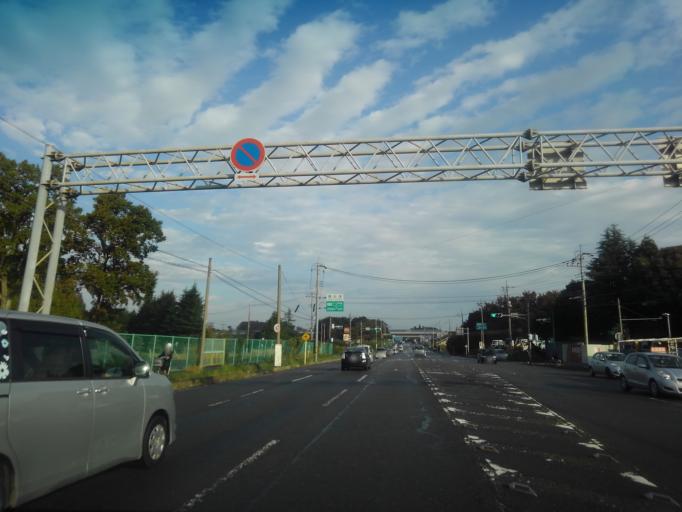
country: JP
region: Ibaraki
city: Naka
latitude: 36.0539
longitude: 140.0846
